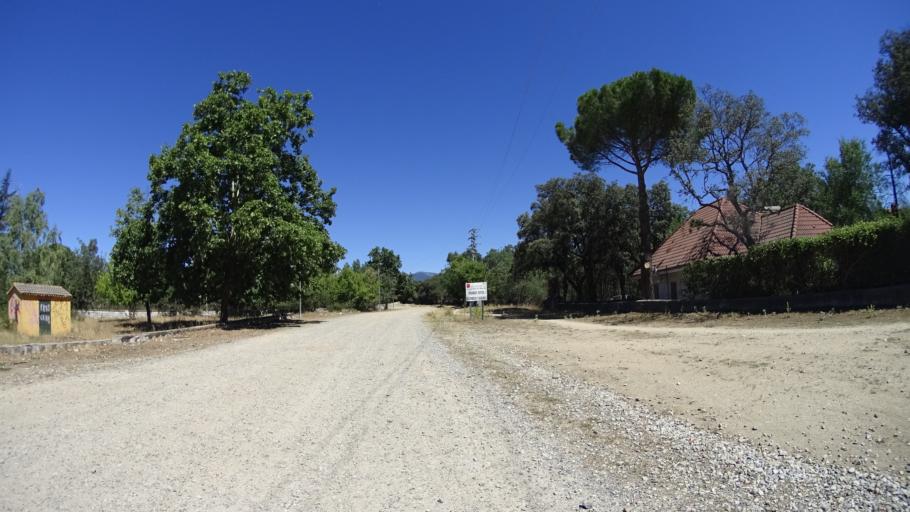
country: ES
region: Madrid
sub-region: Provincia de Madrid
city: Alpedrete
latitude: 40.6463
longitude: -4.0363
